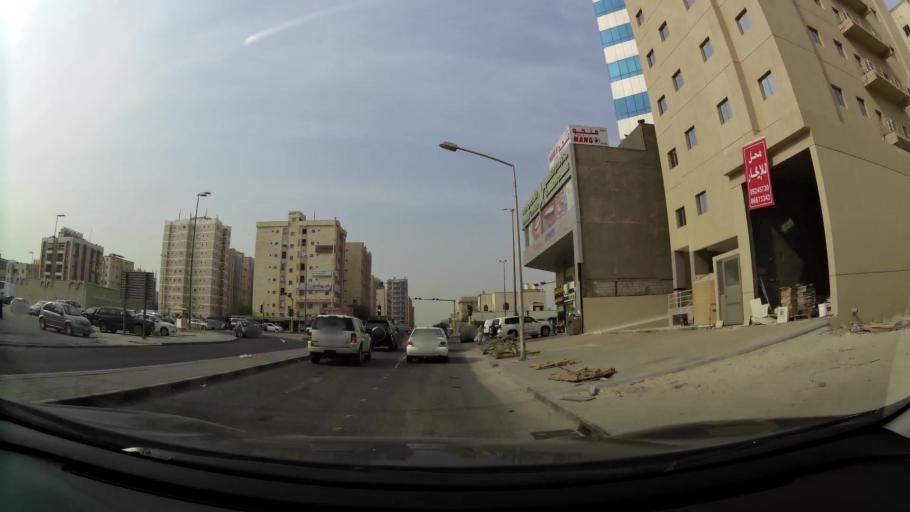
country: KW
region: Al Farwaniyah
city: Al Farwaniyah
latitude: 29.2779
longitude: 47.9541
